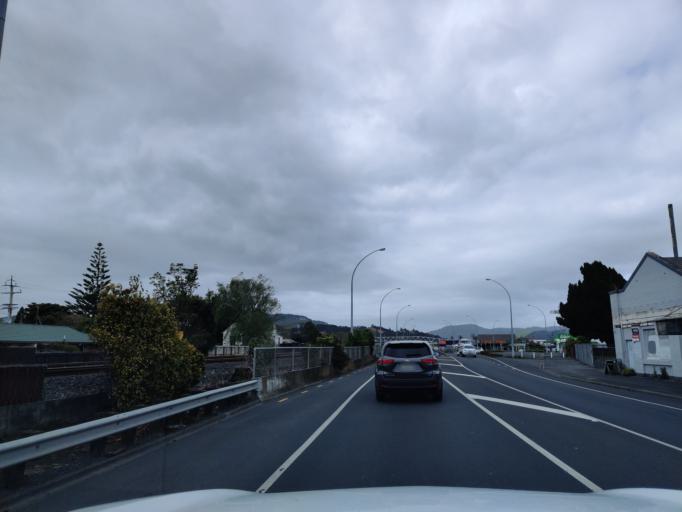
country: NZ
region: Waikato
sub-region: Waikato District
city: Ngaruawahia
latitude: -37.5551
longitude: 175.1592
